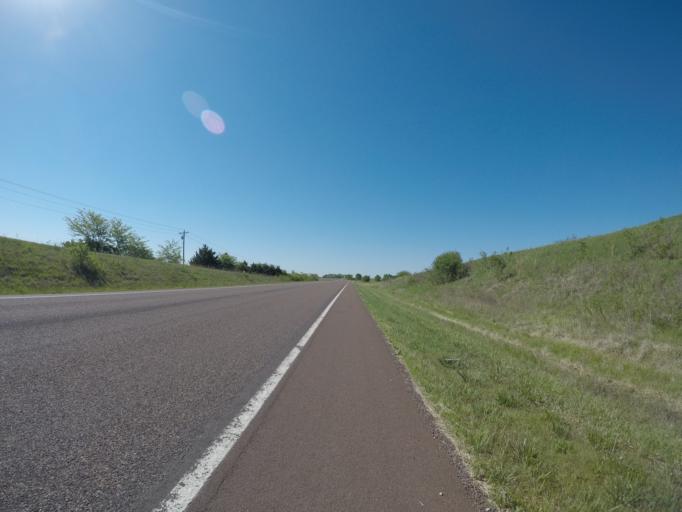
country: US
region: Kansas
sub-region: Osage County
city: Overbrook
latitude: 38.9167
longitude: -95.4561
